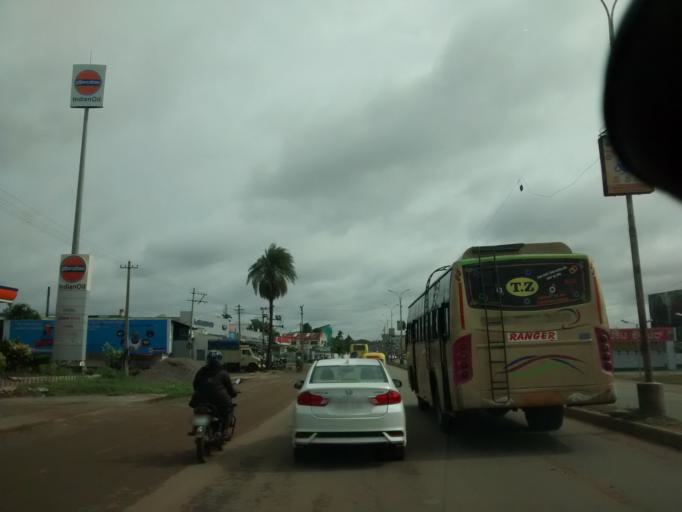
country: IN
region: Karnataka
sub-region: Tumkur
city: Tumkur
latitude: 13.3545
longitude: 77.1033
